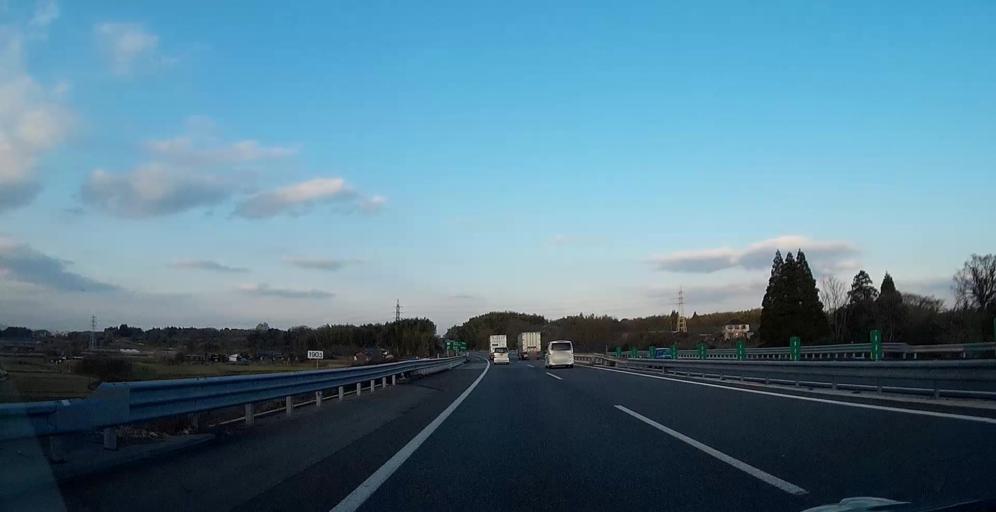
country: JP
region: Kumamoto
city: Uto
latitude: 32.6837
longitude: 130.7337
